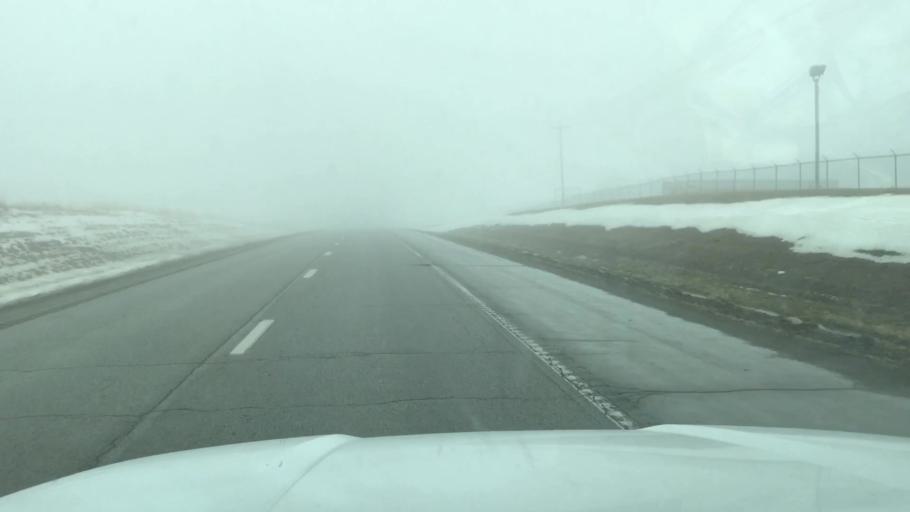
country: US
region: Missouri
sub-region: Clinton County
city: Cameron
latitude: 39.7550
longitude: -94.3012
